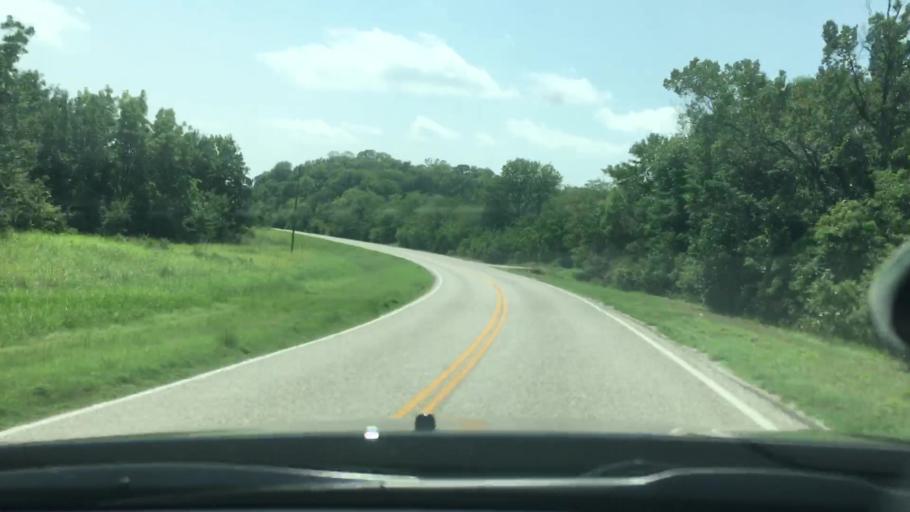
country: US
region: Oklahoma
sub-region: Johnston County
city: Tishomingo
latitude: 34.3755
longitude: -96.4537
